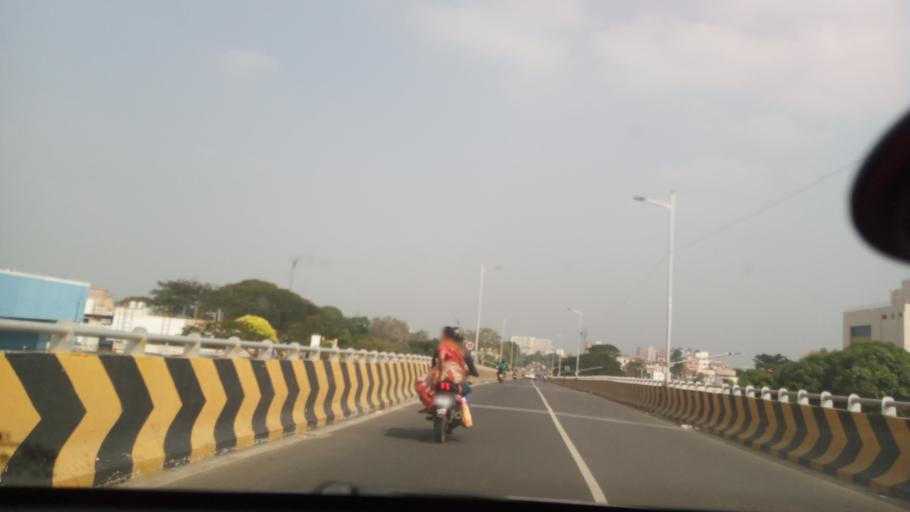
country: IN
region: Tamil Nadu
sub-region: Coimbatore
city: Coimbatore
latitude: 11.0212
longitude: 76.9787
